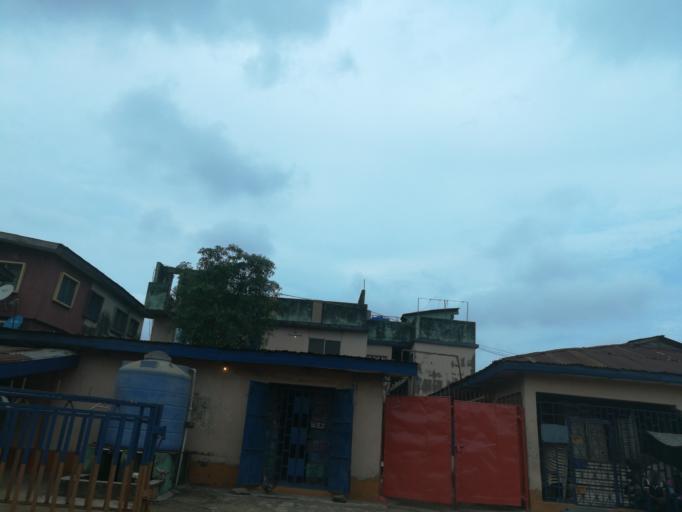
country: NG
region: Lagos
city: Oshodi
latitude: 6.5609
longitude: 3.3442
